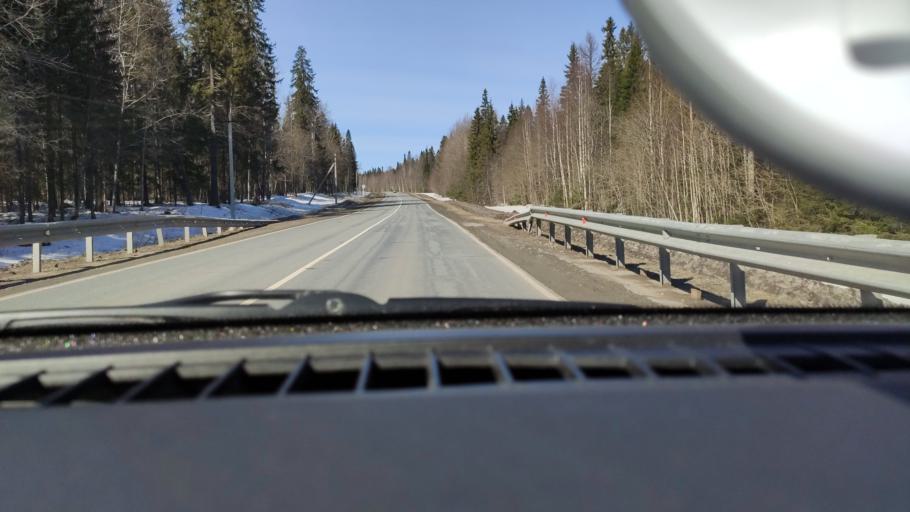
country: RU
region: Perm
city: Perm
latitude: 58.2032
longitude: 56.2021
